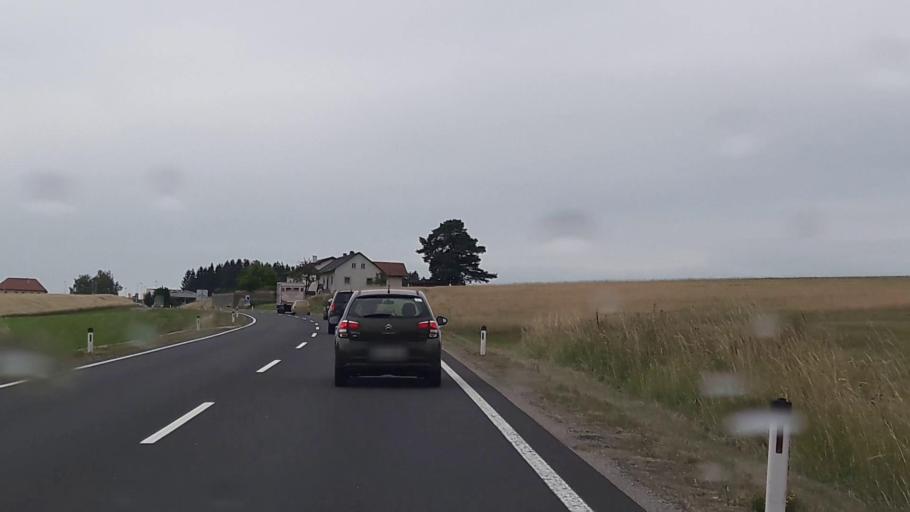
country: AT
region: Upper Austria
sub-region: Politischer Bezirk Rohrbach
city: Kleinzell im Muehlkreis
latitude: 48.4416
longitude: 14.0430
